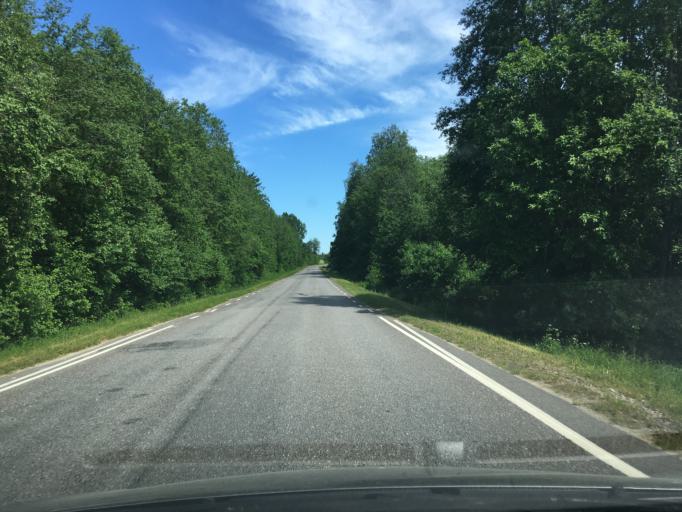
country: EE
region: Raplamaa
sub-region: Rapla vald
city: Rapla
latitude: 59.0511
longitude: 24.8879
